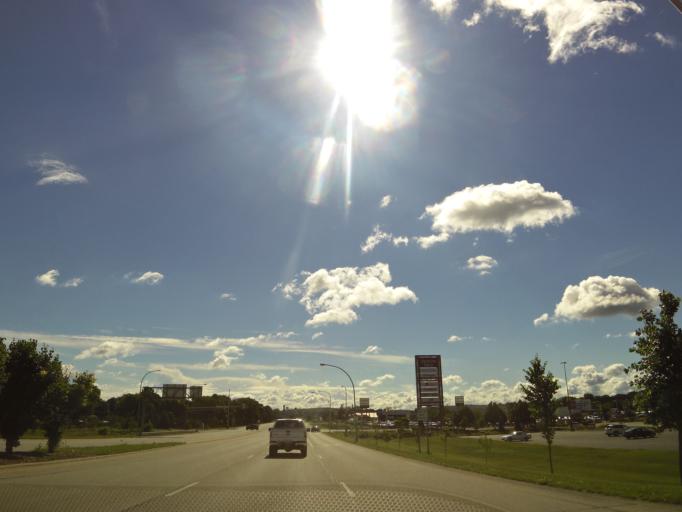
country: US
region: Minnesota
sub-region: Olmsted County
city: Rochester
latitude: 44.0069
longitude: -92.4798
